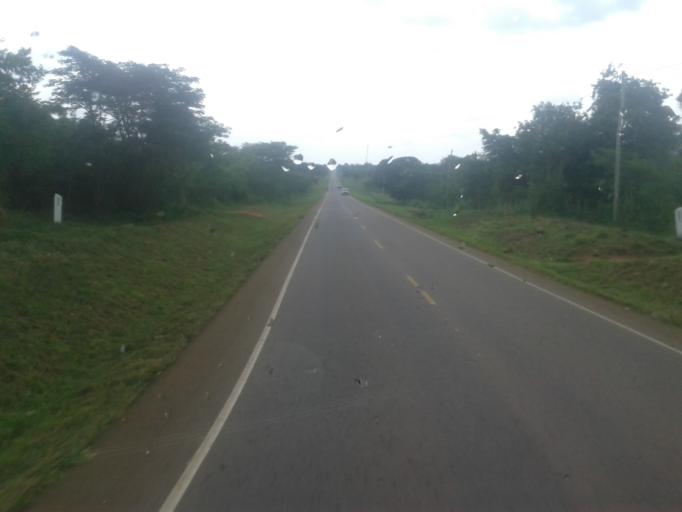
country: UG
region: Central Region
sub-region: Nakasongola District
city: Nakasongola
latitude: 1.3468
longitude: 32.3883
